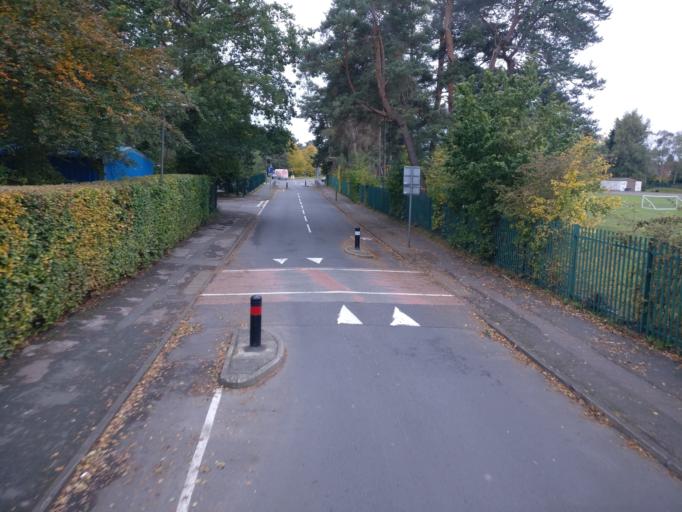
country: GB
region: England
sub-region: Surrey
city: Camberley
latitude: 51.3497
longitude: -0.7227
